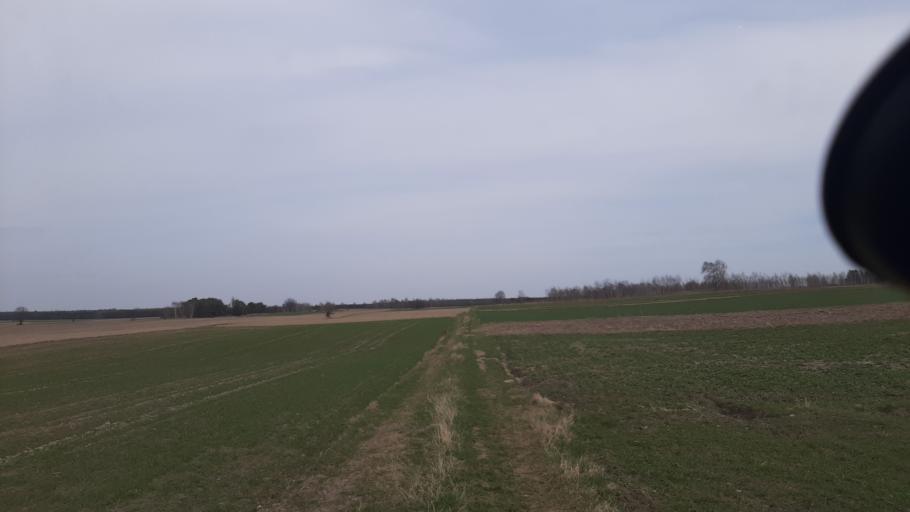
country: PL
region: Lublin Voivodeship
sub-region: Powiat lubelski
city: Jastkow
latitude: 51.3752
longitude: 22.4194
